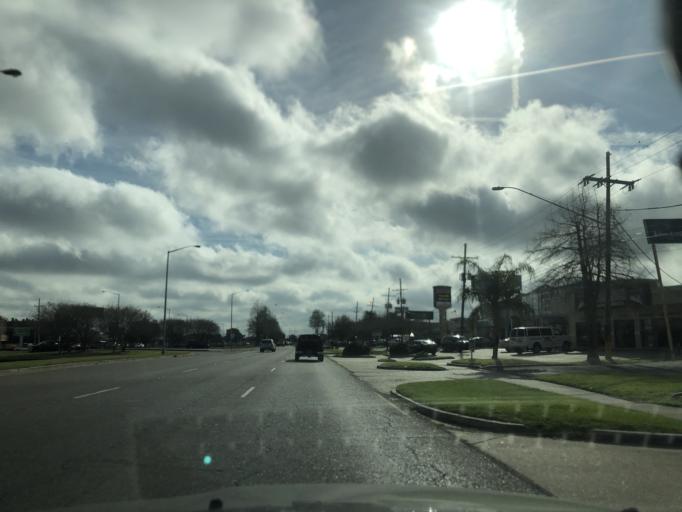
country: US
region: Louisiana
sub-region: Jefferson Parish
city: Kenner
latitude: 30.0058
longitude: -90.1993
